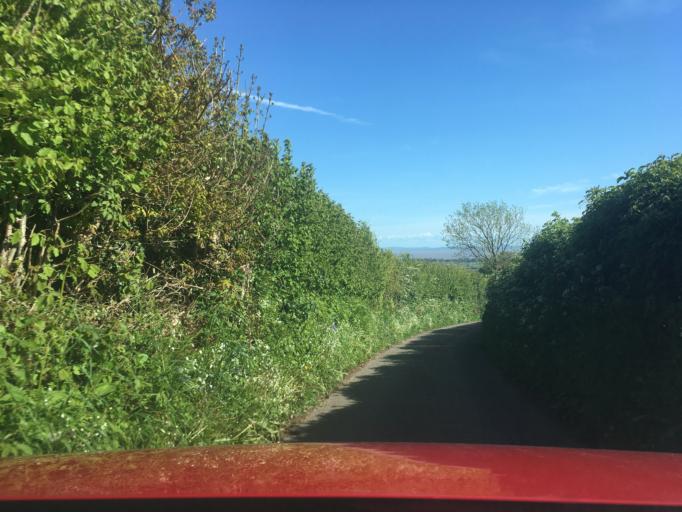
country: GB
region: Wales
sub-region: Newport
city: Marshfield
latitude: 51.5564
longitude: -3.0665
